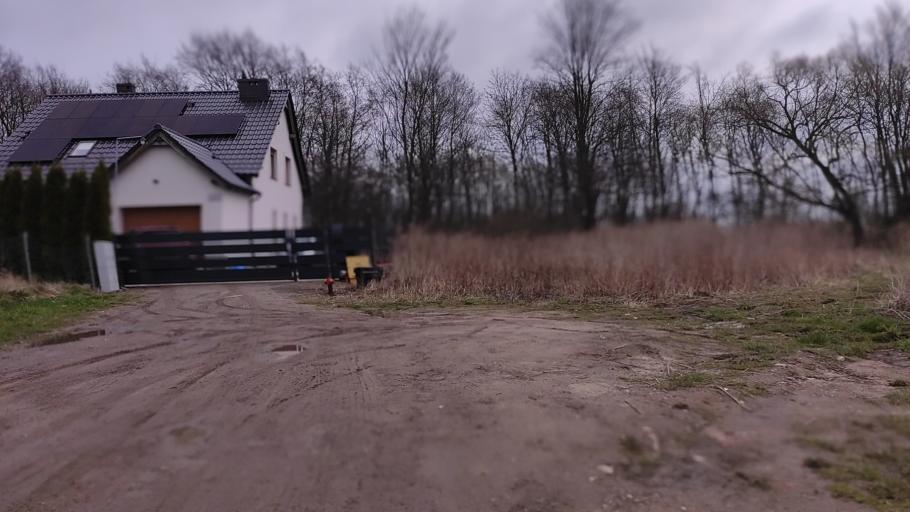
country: PL
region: Greater Poland Voivodeship
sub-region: Powiat poznanski
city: Kostrzyn
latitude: 52.4008
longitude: 17.1741
